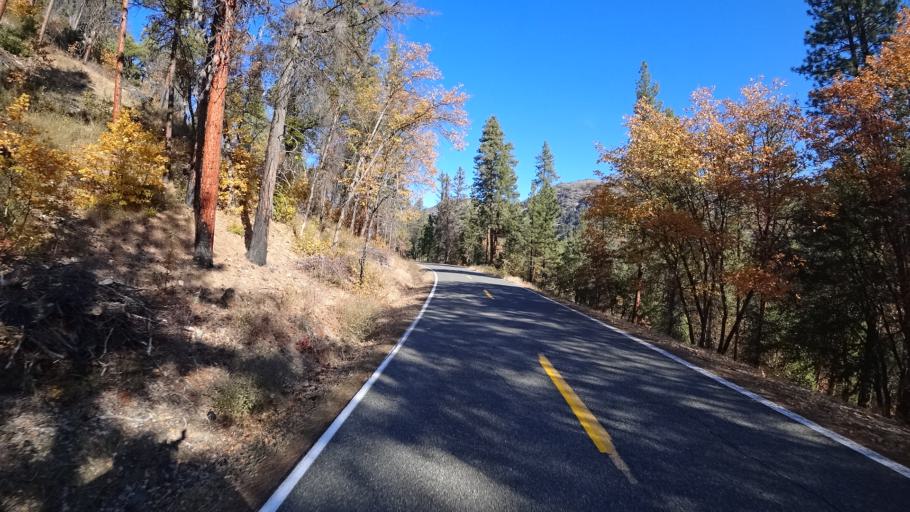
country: US
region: California
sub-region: Siskiyou County
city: Yreka
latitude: 41.8914
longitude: -122.8231
